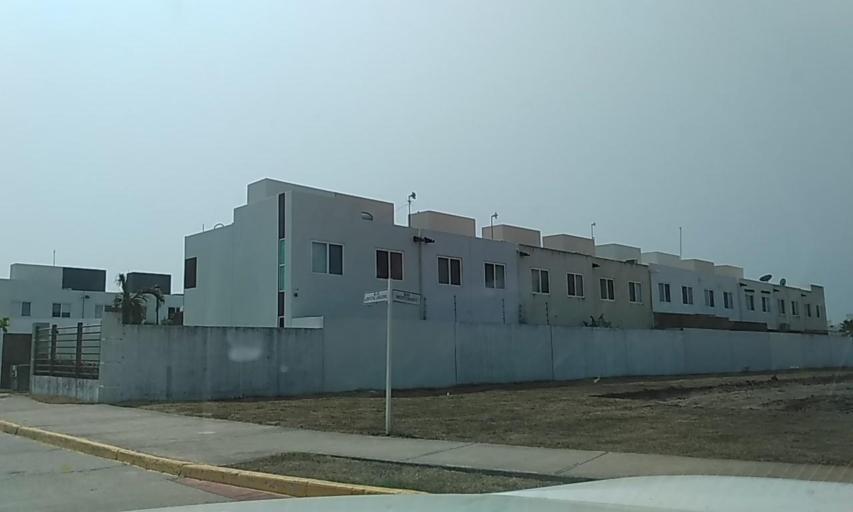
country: MX
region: Veracruz
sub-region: Veracruz
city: Hacienda Sotavento
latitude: 19.1300
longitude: -96.1689
